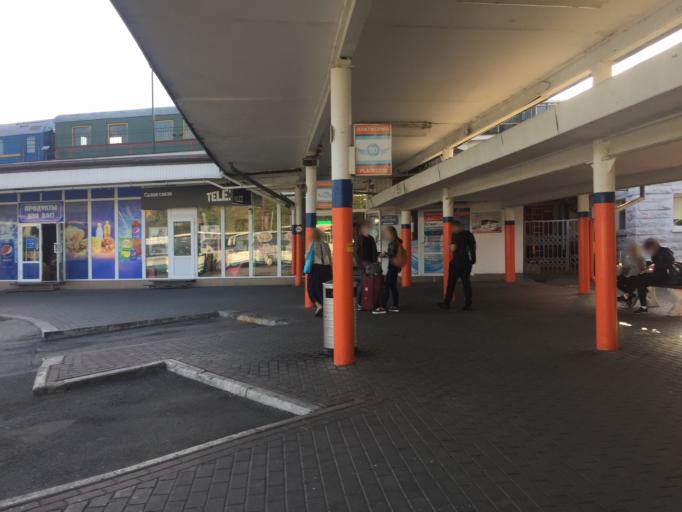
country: RU
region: Kaliningrad
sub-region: Gorod Kaliningrad
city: Kaliningrad
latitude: 54.6934
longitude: 20.5021
